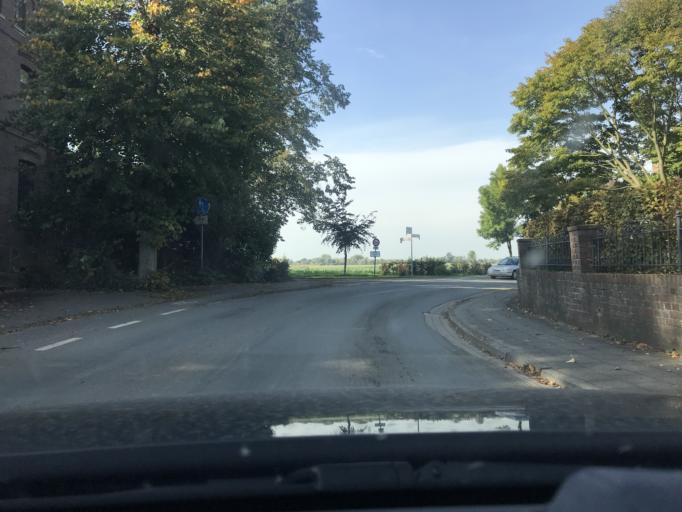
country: DE
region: North Rhine-Westphalia
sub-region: Regierungsbezirk Dusseldorf
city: Emmerich
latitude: 51.7901
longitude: 6.2317
